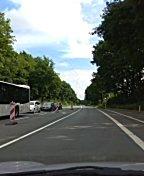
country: DE
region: North Rhine-Westphalia
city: Ibbenburen
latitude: 52.2847
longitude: 7.7483
